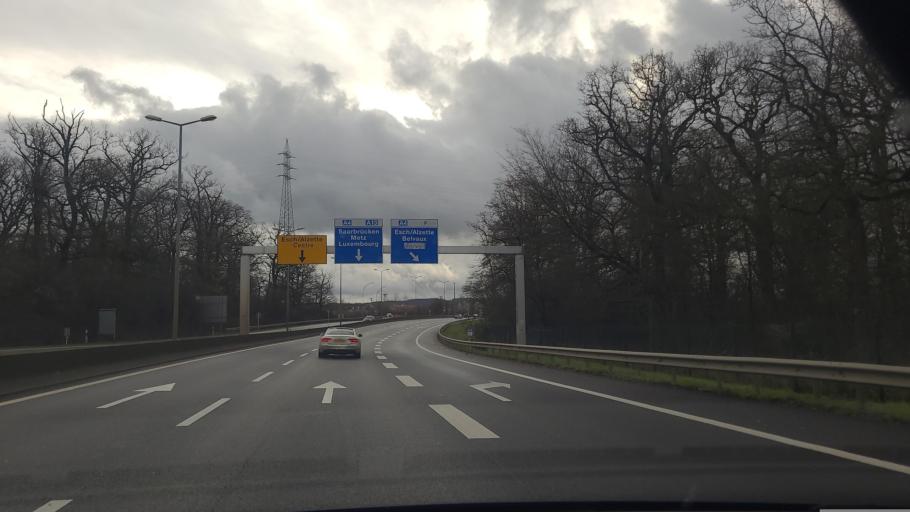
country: LU
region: Luxembourg
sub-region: Canton d'Esch-sur-Alzette
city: Esch-sur-Alzette
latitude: 49.5152
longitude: 5.9744
